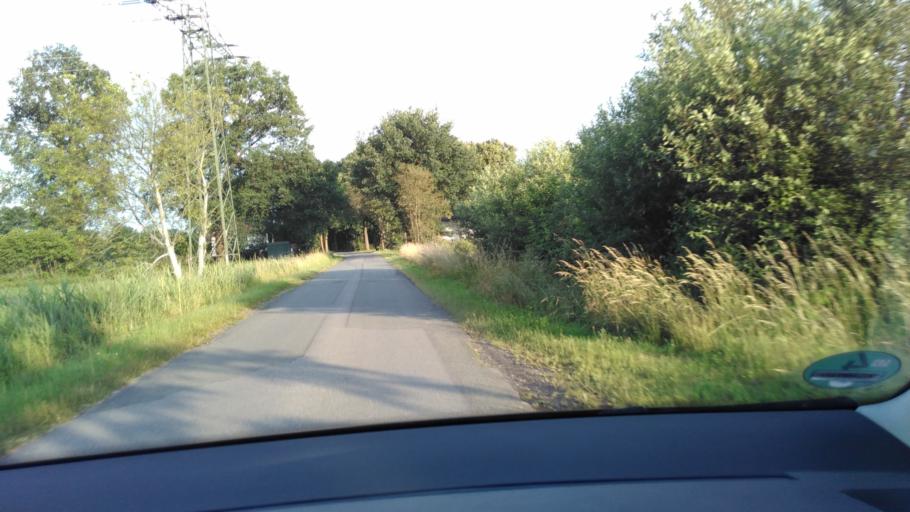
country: DE
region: North Rhine-Westphalia
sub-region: Regierungsbezirk Detmold
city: Verl
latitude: 51.8668
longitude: 8.5109
